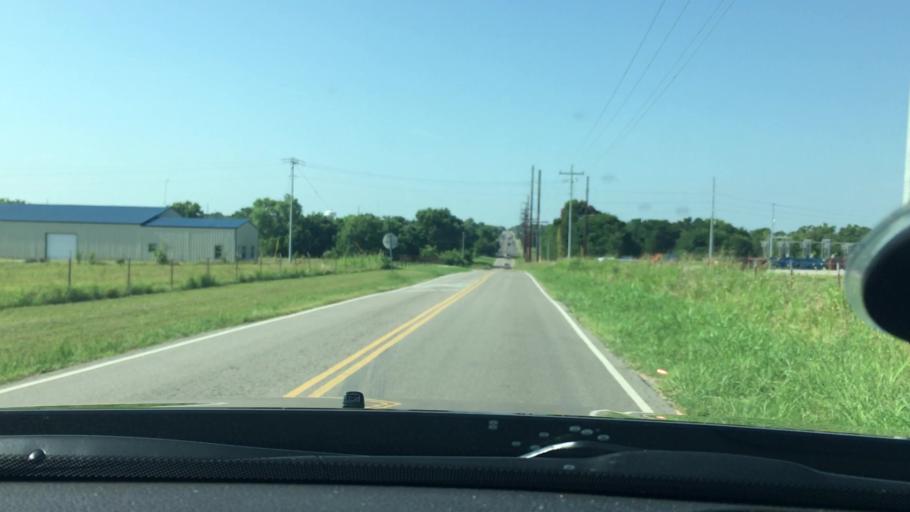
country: US
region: Oklahoma
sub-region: Pontotoc County
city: Ada
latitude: 34.7949
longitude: -96.6348
